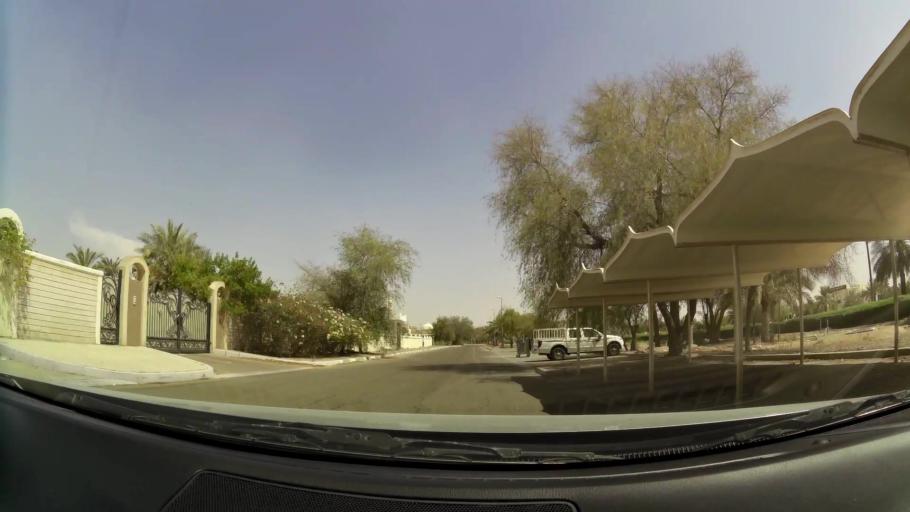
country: AE
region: Abu Dhabi
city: Al Ain
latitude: 24.2323
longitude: 55.7081
